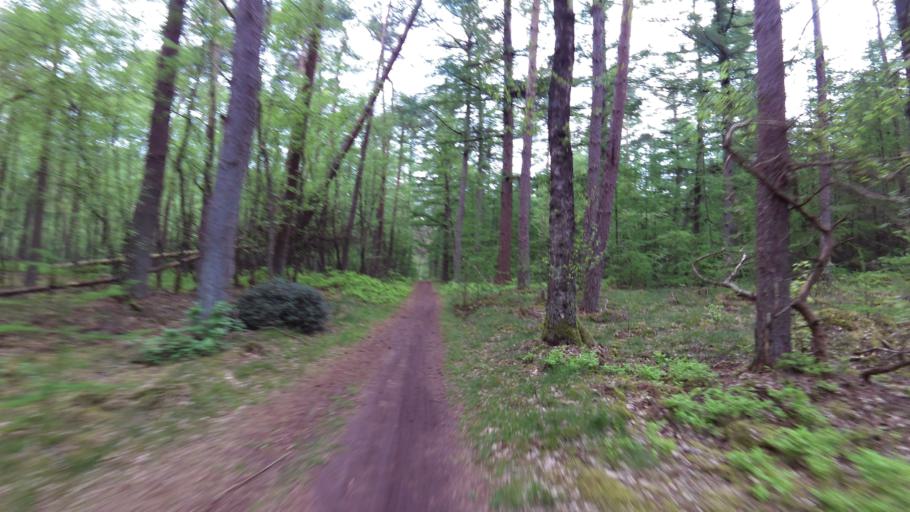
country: NL
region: Gelderland
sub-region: Gemeente Brummen
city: Eerbeek
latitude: 52.0772
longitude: 6.0505
